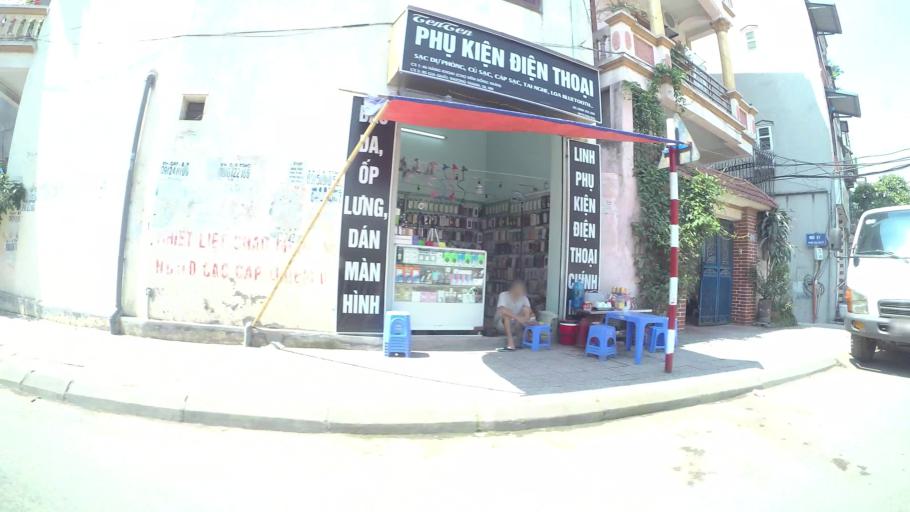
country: VN
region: Ha Noi
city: Hoan Kiem
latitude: 21.0535
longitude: 105.8780
